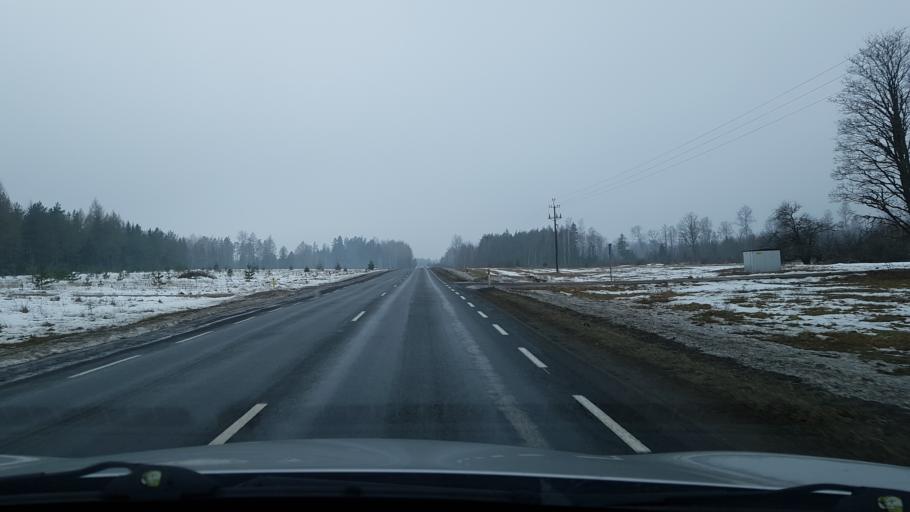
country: EE
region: Viljandimaa
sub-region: Viiratsi vald
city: Viiratsi
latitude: 58.2484
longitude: 25.7767
